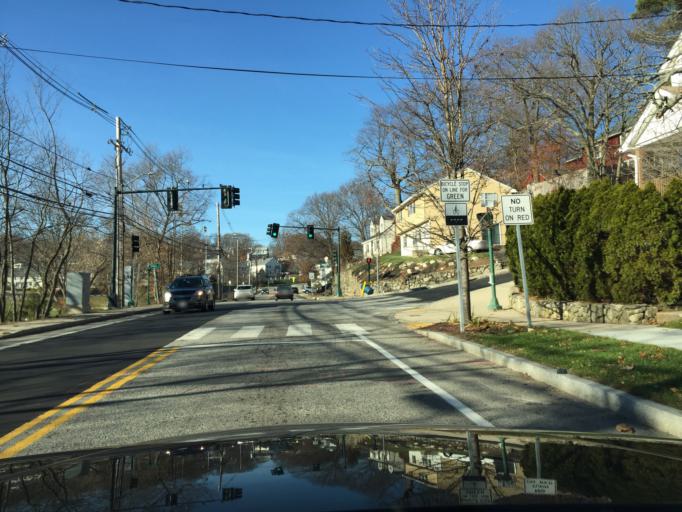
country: US
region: Massachusetts
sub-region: Middlesex County
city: Arlington
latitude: 42.4259
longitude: -71.1722
